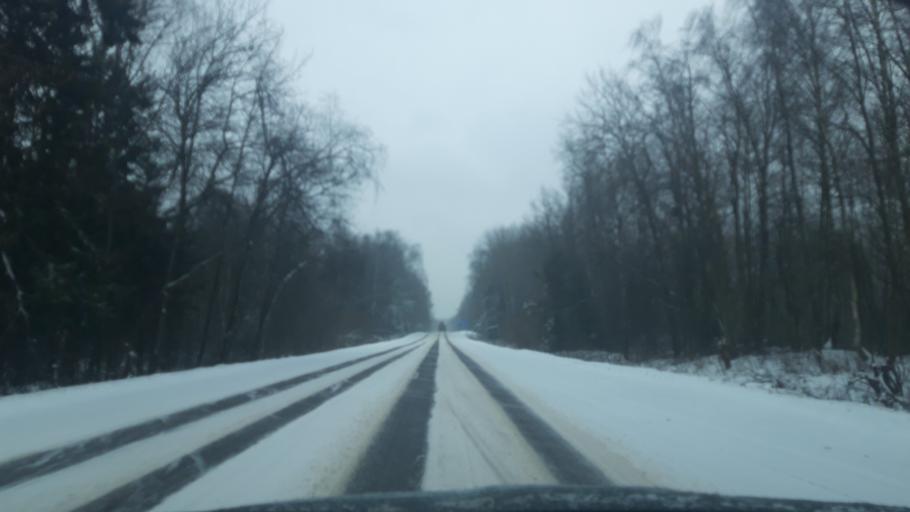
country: RU
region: Moskovskaya
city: Avtopoligon
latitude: 56.2736
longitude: 37.3647
